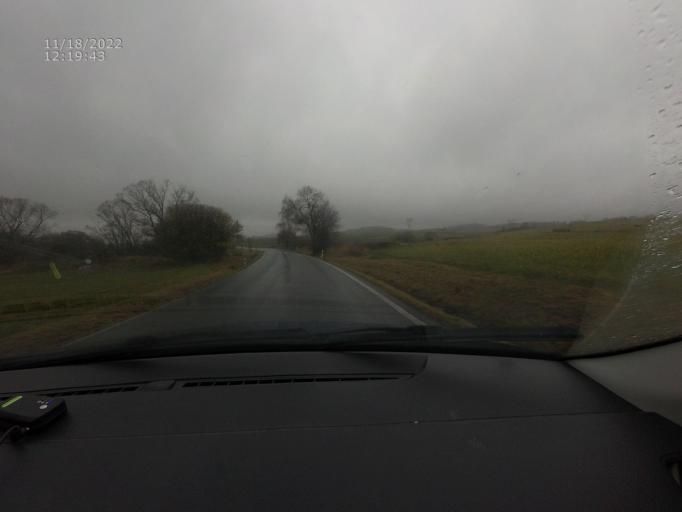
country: CZ
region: Plzensky
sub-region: Okres Plzen-Jih
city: Nepomuk
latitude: 49.4776
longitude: 13.5688
